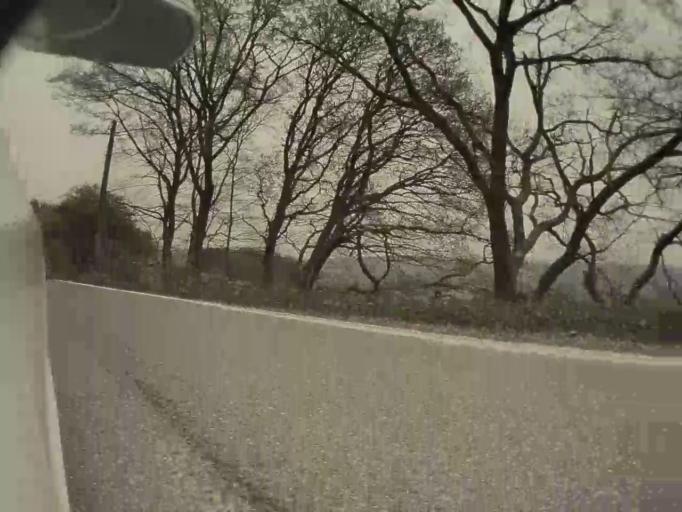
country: BE
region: Wallonia
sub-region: Province du Luxembourg
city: La Roche-en-Ardenne
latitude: 50.2247
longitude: 5.6232
